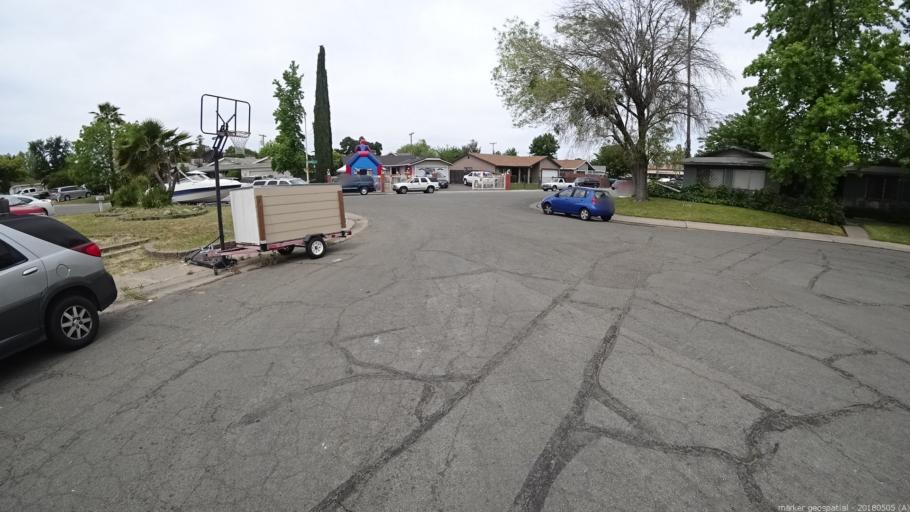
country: US
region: California
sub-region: Sacramento County
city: Rio Linda
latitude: 38.6425
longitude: -121.4592
